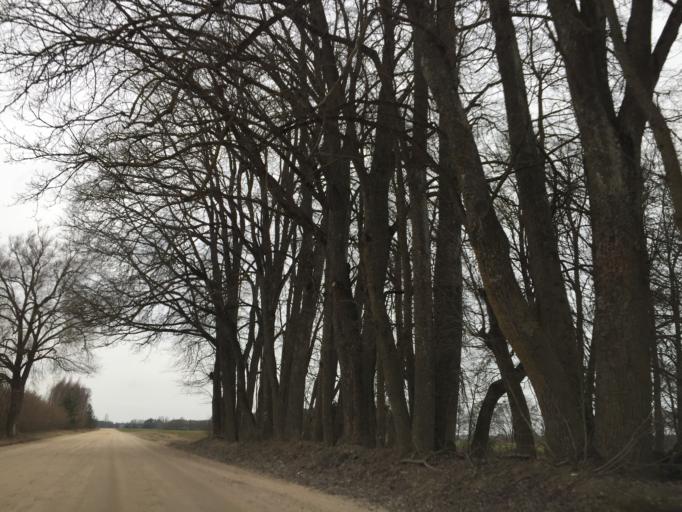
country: LV
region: Livani
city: Livani
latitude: 56.3084
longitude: 26.1662
